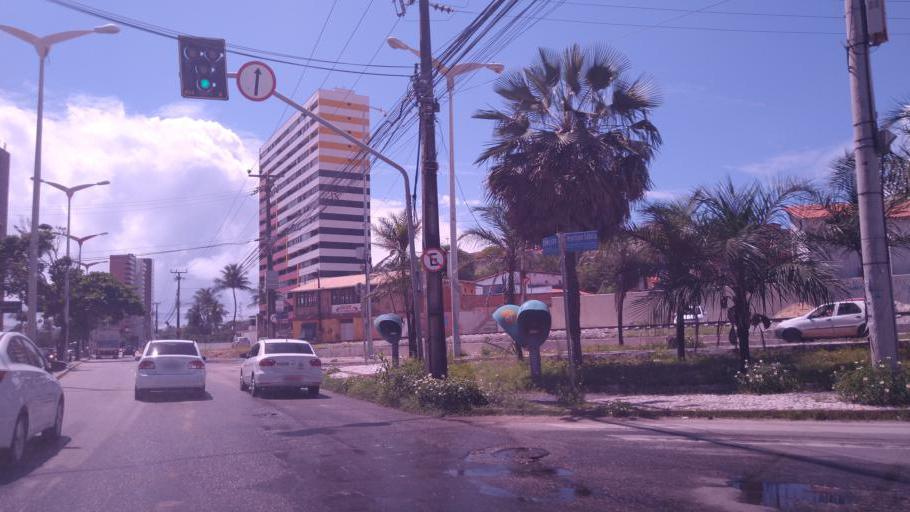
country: BR
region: Ceara
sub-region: Fortaleza
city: Fortaleza
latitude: -3.7229
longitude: -38.4800
